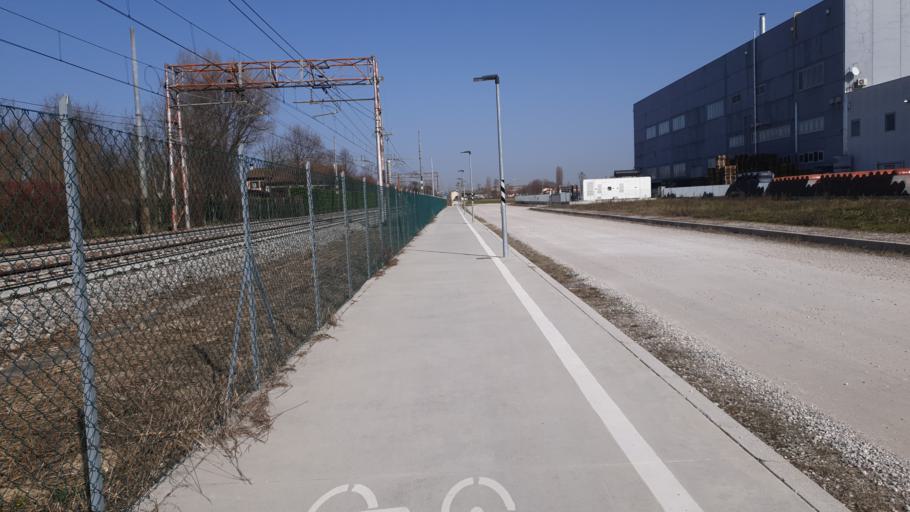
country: IT
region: Veneto
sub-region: Provincia di Padova
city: Camposampiero
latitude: 45.5462
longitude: 11.9191
